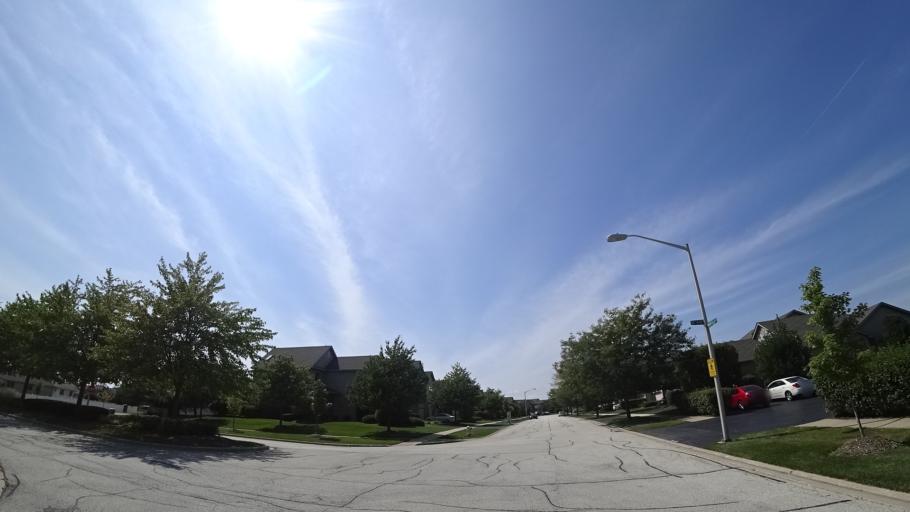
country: US
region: Illinois
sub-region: Cook County
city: Orland Hills
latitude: 41.5584
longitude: -87.8398
